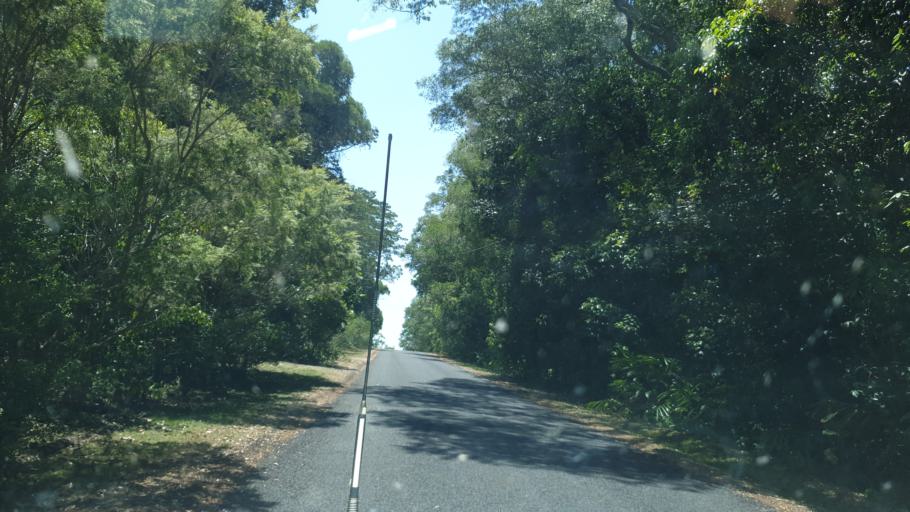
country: AU
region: Queensland
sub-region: Tablelands
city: Atherton
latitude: -17.3415
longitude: 145.6272
